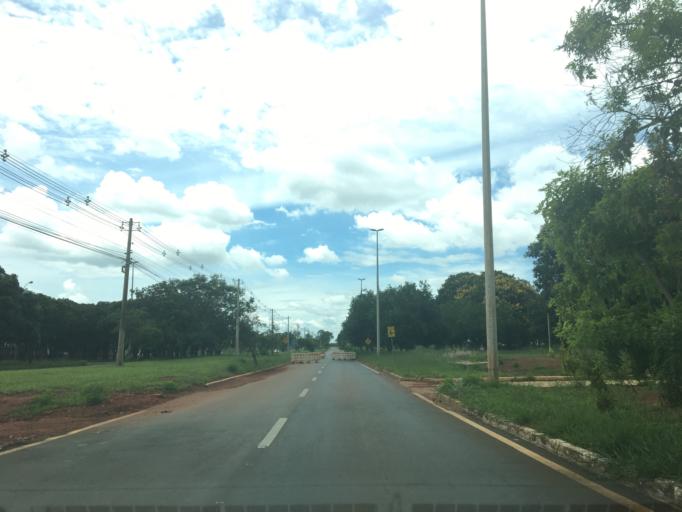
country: BR
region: Federal District
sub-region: Brasilia
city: Brasilia
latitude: -15.8292
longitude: -47.9370
